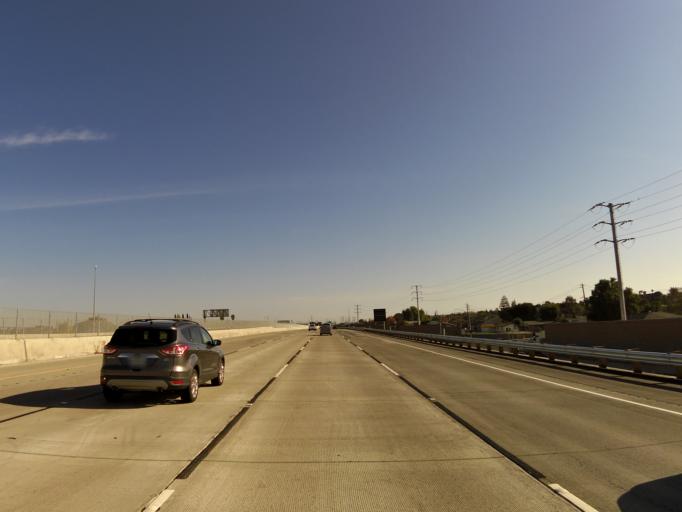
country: US
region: California
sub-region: Contra Costa County
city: Antioch
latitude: 37.9981
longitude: -121.8079
